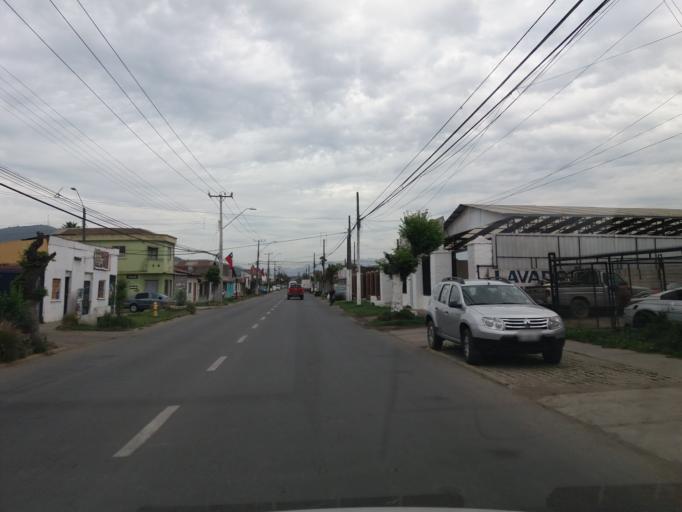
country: CL
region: Valparaiso
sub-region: Provincia de Quillota
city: Hacienda La Calera
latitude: -32.7757
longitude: -71.1919
